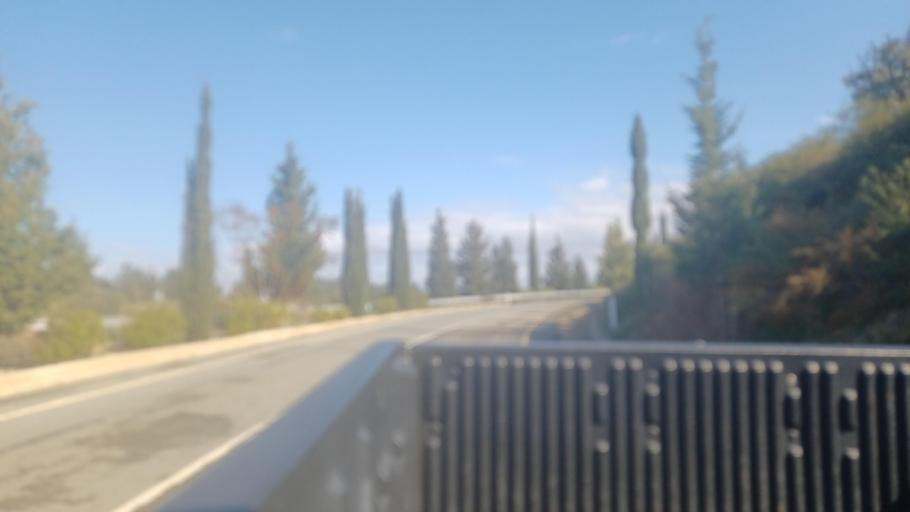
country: CY
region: Limassol
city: Pissouri
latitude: 34.7121
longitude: 32.5796
